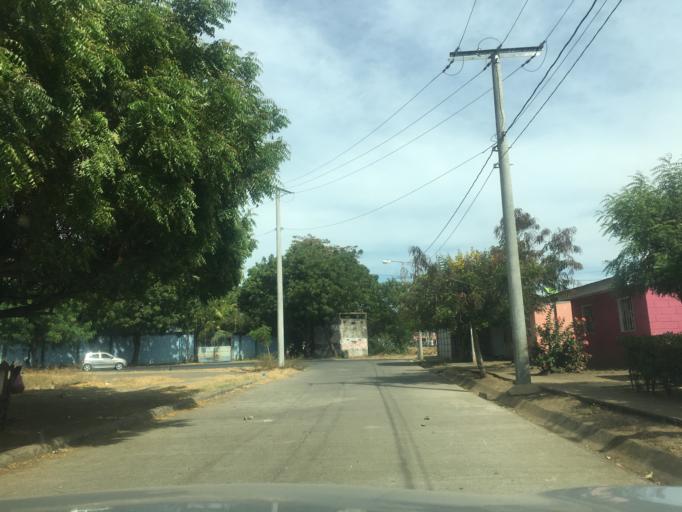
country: NI
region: Managua
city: Managua
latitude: 12.1604
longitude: -86.2760
